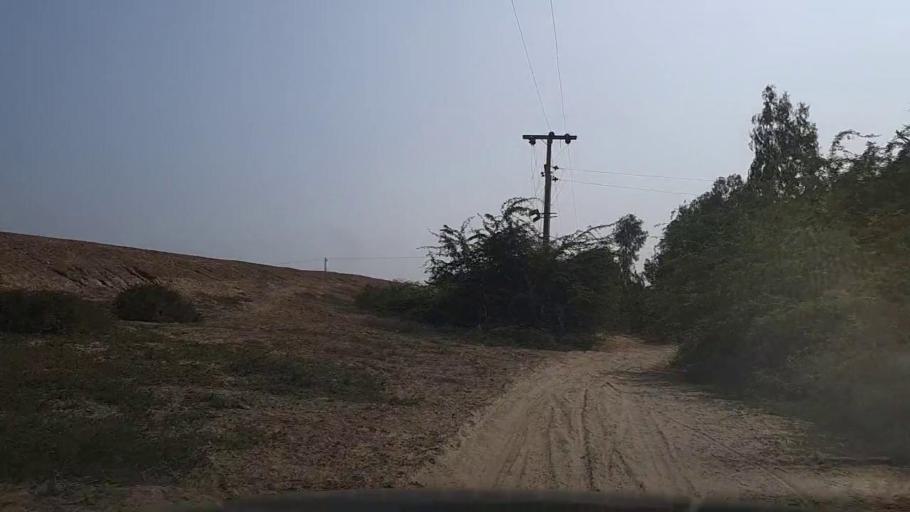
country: PK
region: Sindh
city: Chuhar Jamali
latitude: 24.5524
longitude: 67.9178
